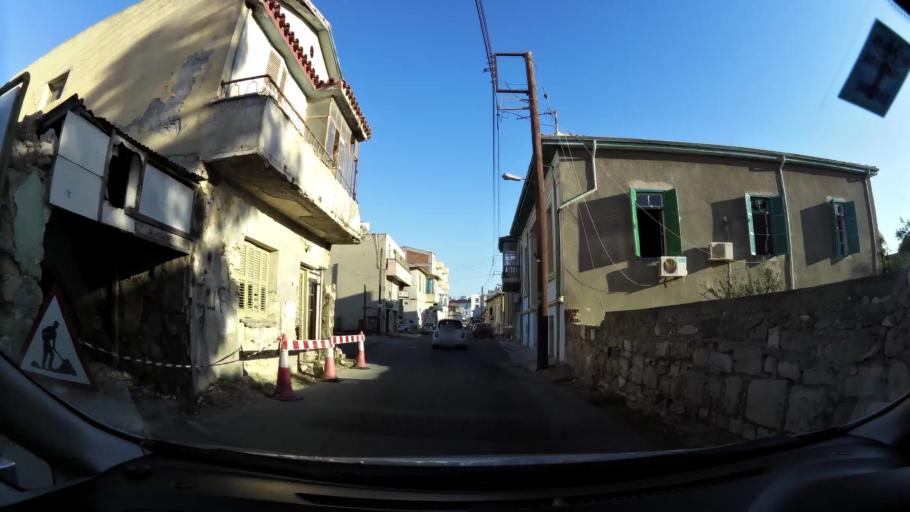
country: CY
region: Larnaka
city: Larnaca
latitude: 34.9097
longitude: 33.6357
